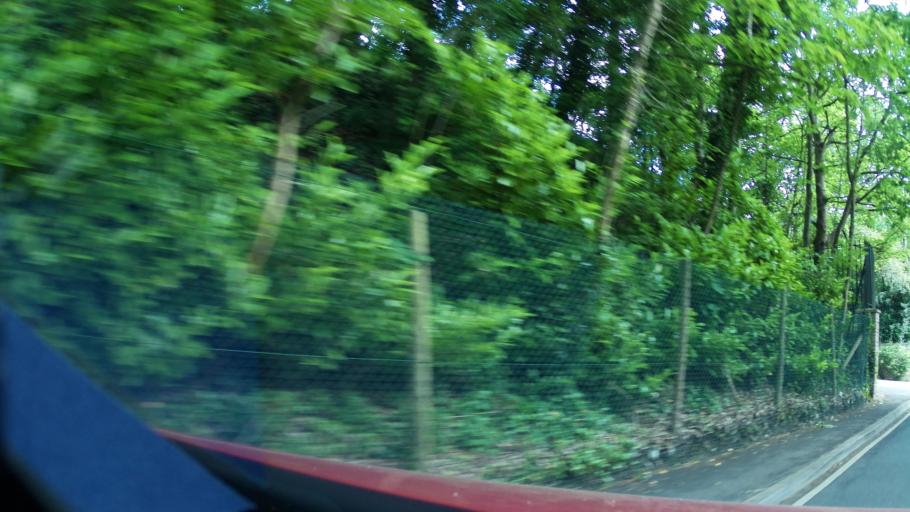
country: GB
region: England
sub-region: South Gloucestershire
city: Kingswood
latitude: 51.4476
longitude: -2.5343
